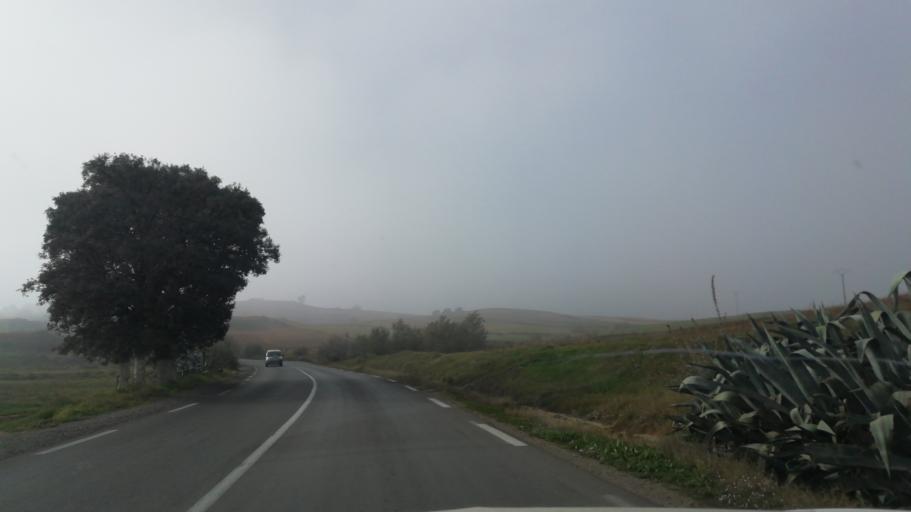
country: DZ
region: Mascara
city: Mascara
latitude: 35.5352
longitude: 0.3546
